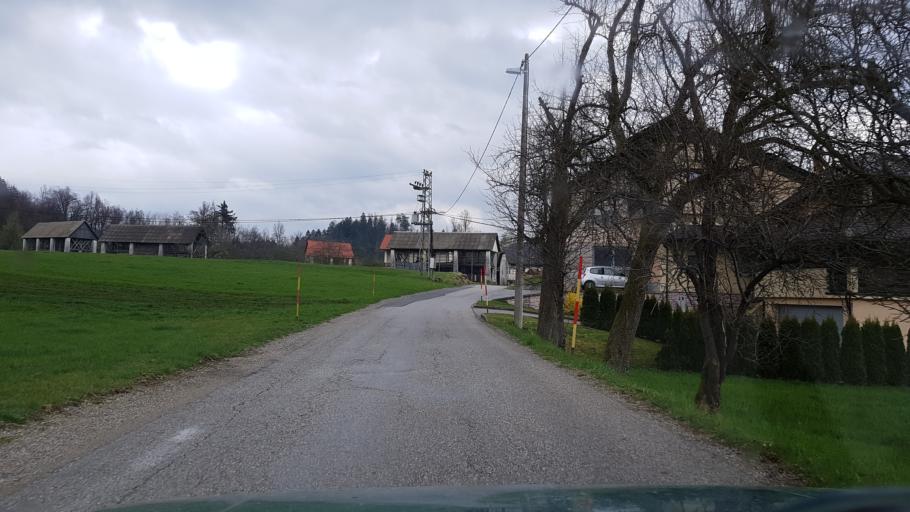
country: SI
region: Tolmin
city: Tolmin
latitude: 46.1106
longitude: 13.8461
